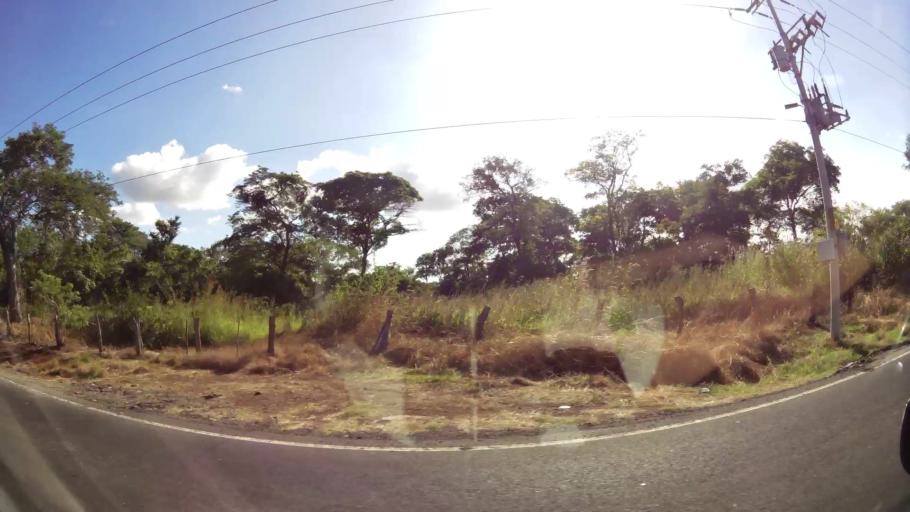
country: CR
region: Guanacaste
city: Sardinal
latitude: 10.5889
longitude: -85.6400
